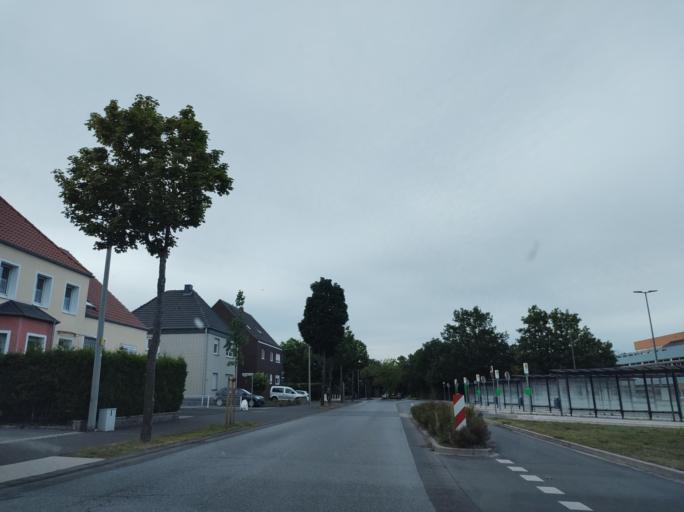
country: DE
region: North Rhine-Westphalia
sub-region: Regierungsbezirk Detmold
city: Salzkotten
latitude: 51.6595
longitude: 8.6017
